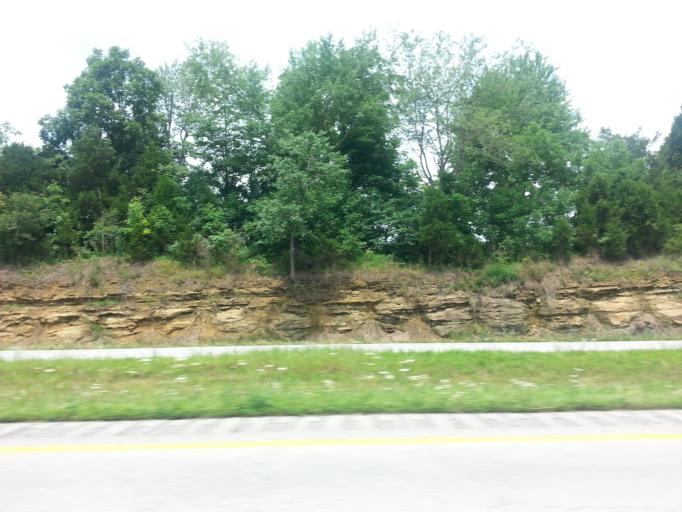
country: US
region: Kentucky
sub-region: Grayson County
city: Leitchfield
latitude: 37.5421
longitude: -86.1288
